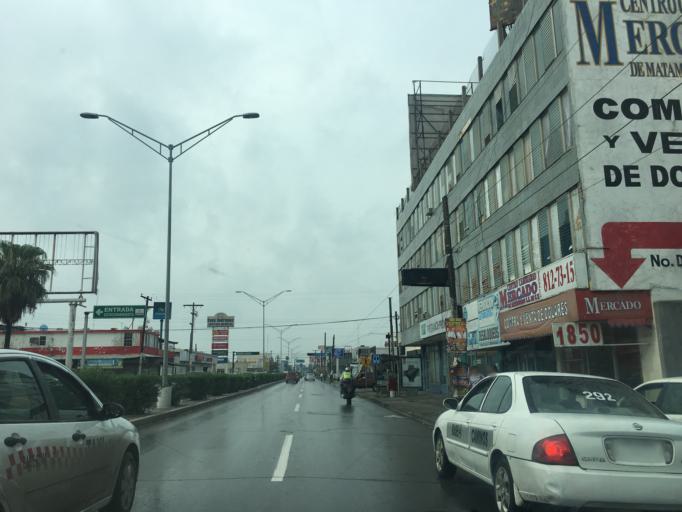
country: MX
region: Tamaulipas
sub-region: Matamoros
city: Heroica Matamoros
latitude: 25.8700
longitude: -97.5040
